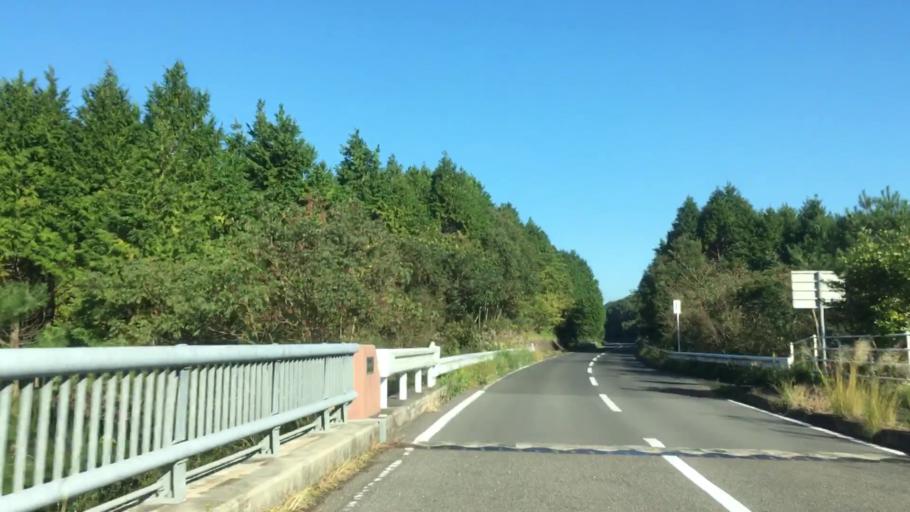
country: JP
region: Nagasaki
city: Sasebo
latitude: 33.0289
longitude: 129.6903
